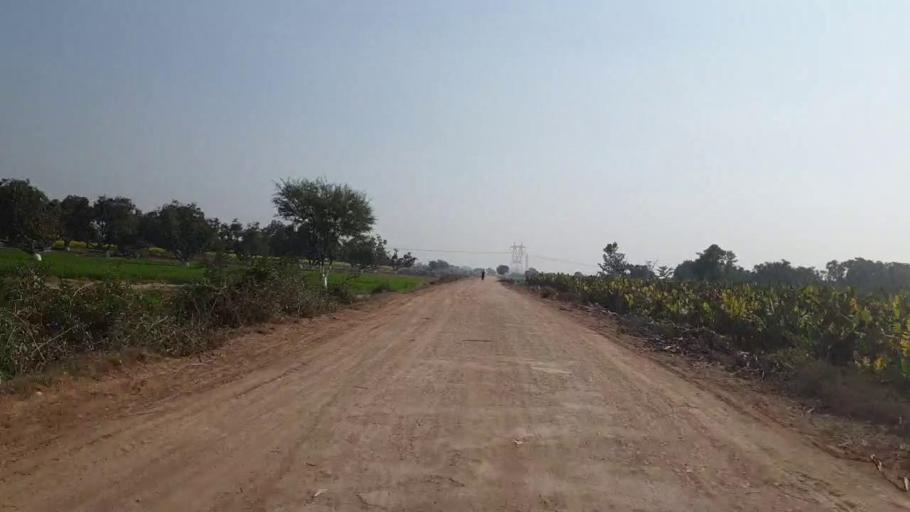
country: PK
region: Sindh
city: Bhit Shah
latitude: 25.7259
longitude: 68.5356
